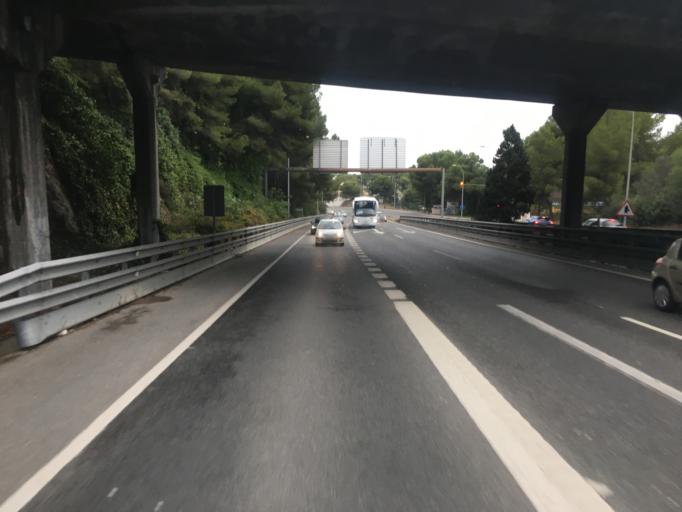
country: ES
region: Balearic Islands
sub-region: Illes Balears
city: Palma
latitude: 39.5529
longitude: 2.6162
